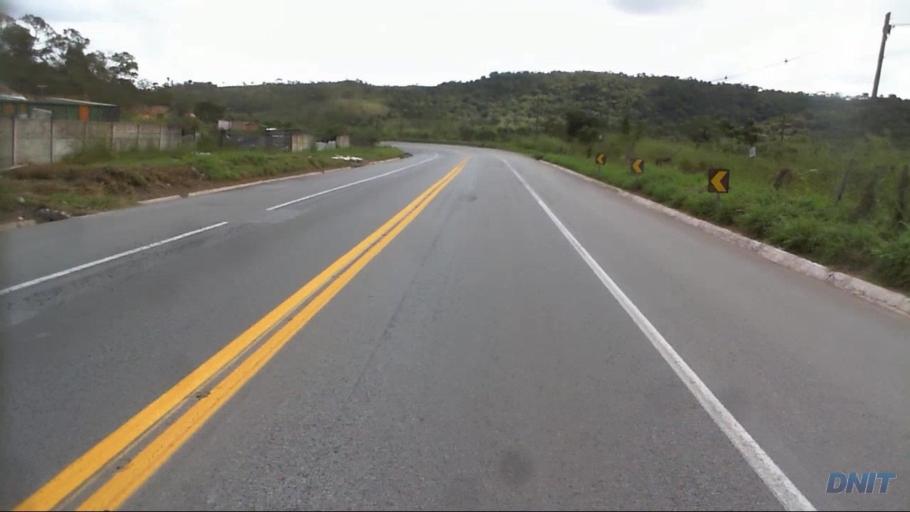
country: BR
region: Minas Gerais
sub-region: Santa Luzia
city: Santa Luzia
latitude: -19.8155
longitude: -43.8083
